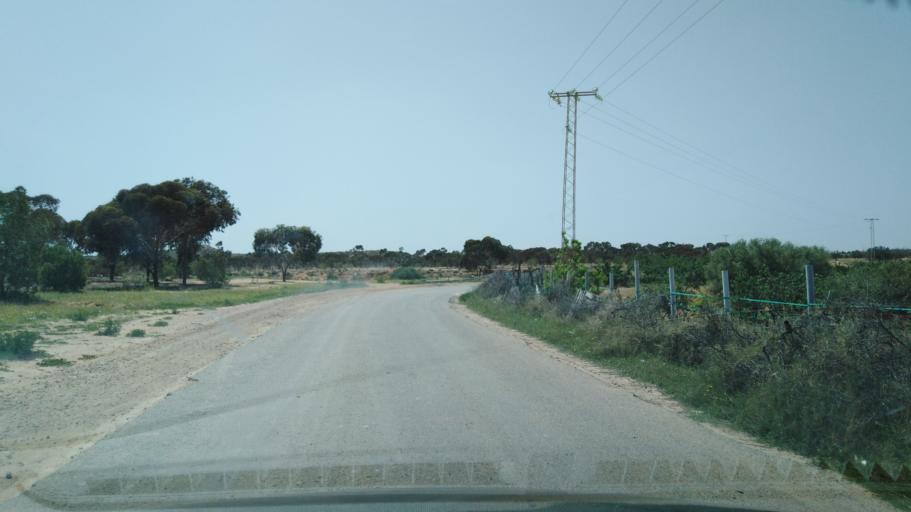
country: TN
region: Safaqis
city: Sfax
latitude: 34.7180
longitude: 10.5319
